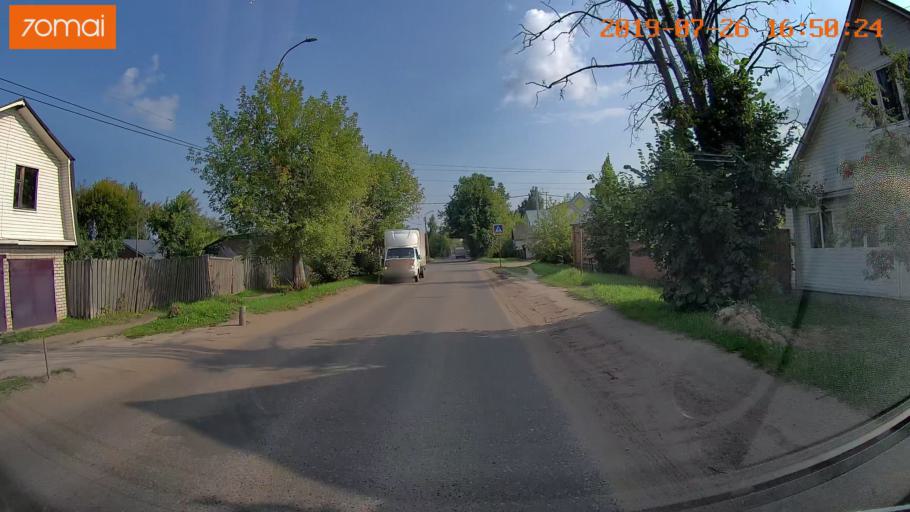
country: RU
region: Ivanovo
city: Bogorodskoye
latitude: 57.0242
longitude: 41.0207
